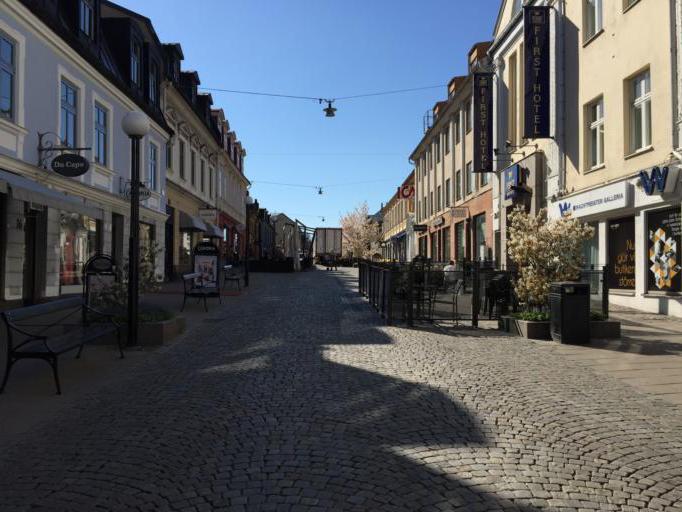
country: SE
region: Blekinge
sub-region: Karlskrona Kommun
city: Karlskrona
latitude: 56.1616
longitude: 15.5838
